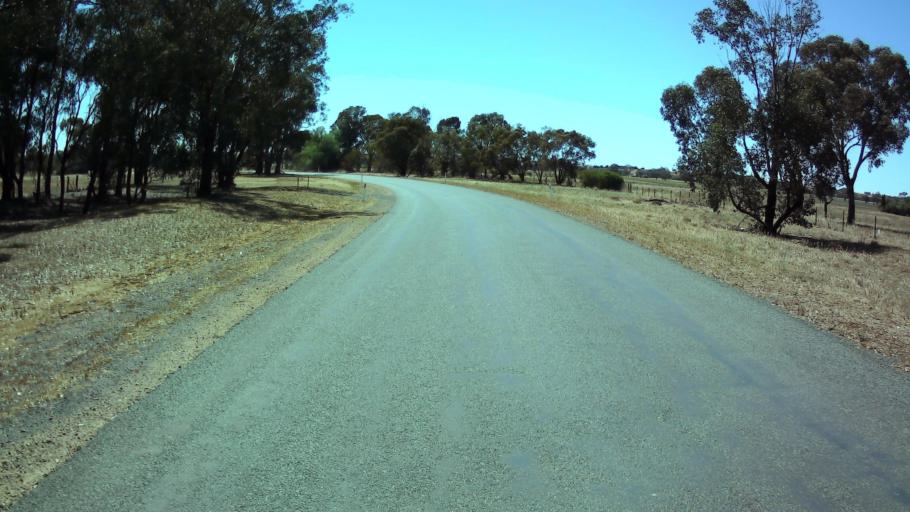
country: AU
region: New South Wales
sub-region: Weddin
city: Grenfell
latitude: -34.0022
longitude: 148.3846
